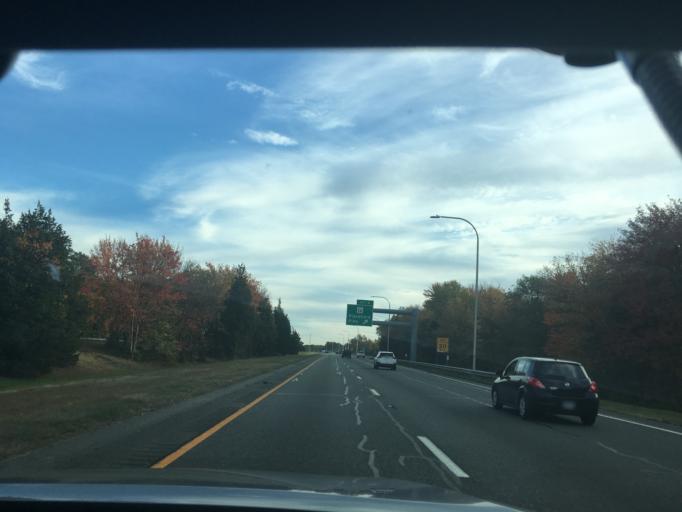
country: US
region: Rhode Island
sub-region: Providence County
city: Johnston
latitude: 41.7938
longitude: -71.5086
